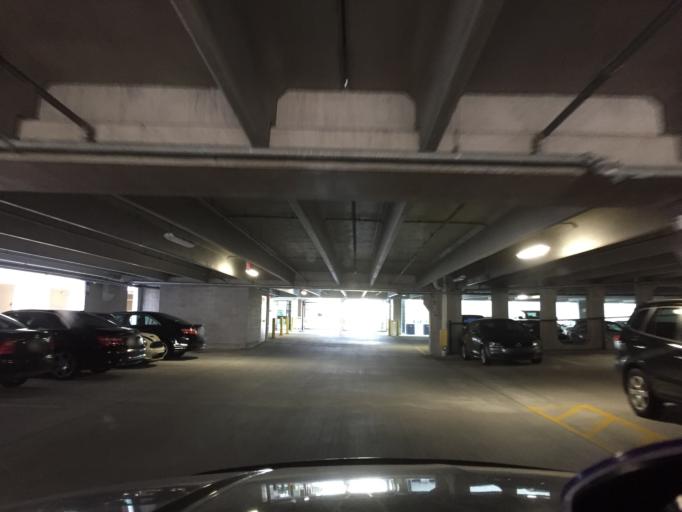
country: US
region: Florida
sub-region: Orange County
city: Oak Ridge
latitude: 28.4824
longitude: -81.4300
